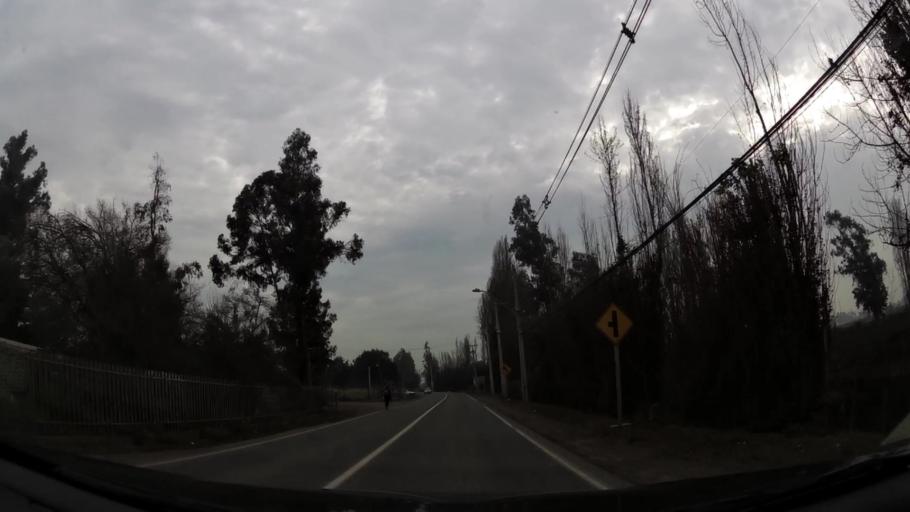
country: CL
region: Santiago Metropolitan
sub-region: Provincia de Chacabuco
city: Chicureo Abajo
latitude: -33.2480
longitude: -70.7637
